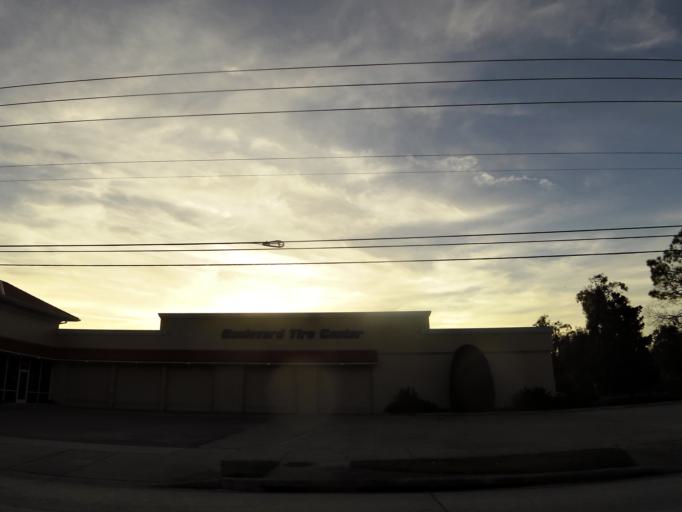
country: US
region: Florida
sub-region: Volusia County
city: De Land Southwest
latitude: 29.0147
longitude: -81.3030
